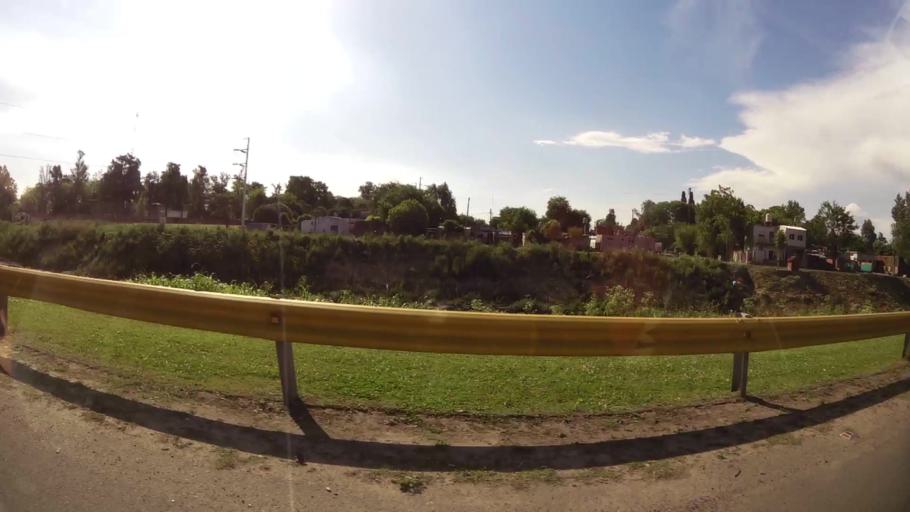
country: AR
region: Buenos Aires
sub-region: Partido de Merlo
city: Merlo
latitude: -34.6538
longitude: -58.7486
